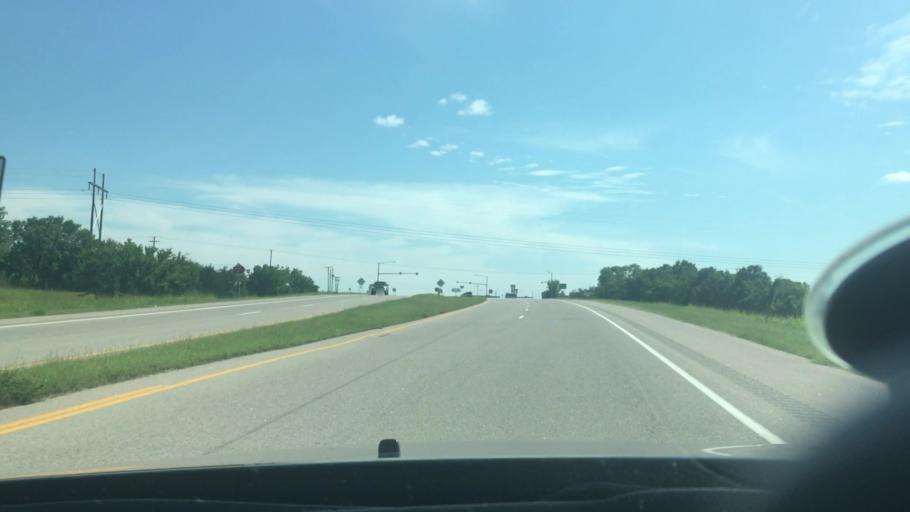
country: US
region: Oklahoma
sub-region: Seminole County
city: Konawa
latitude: 34.9443
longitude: -96.6823
